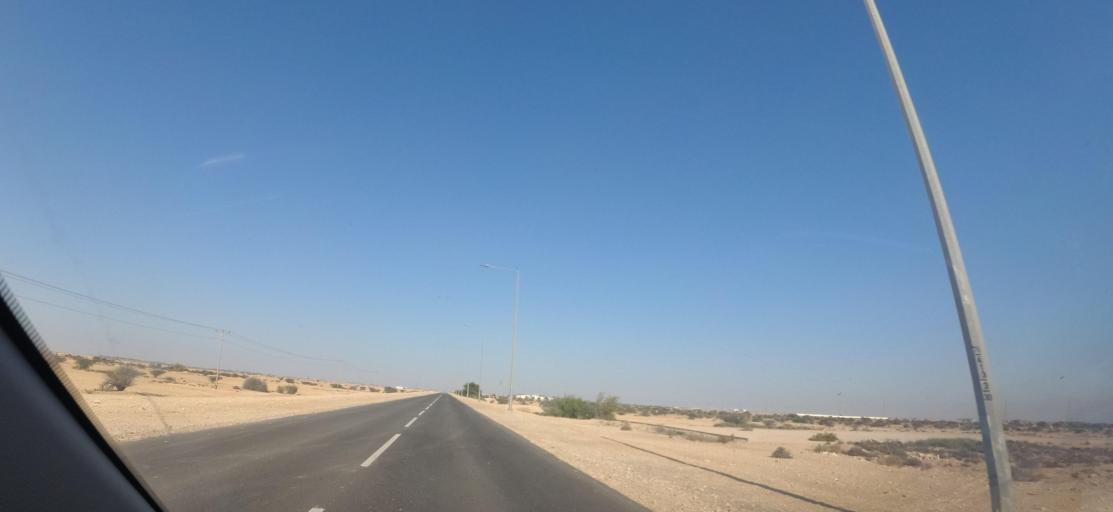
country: QA
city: Al Ghuwayriyah
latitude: 25.8385
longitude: 51.2586
